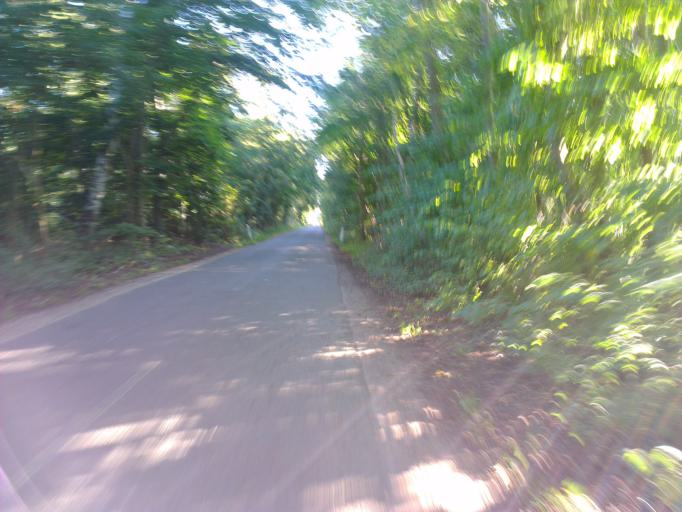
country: DK
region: Capital Region
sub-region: Frederikssund Kommune
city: Jaegerspris
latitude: 55.8147
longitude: 11.9343
